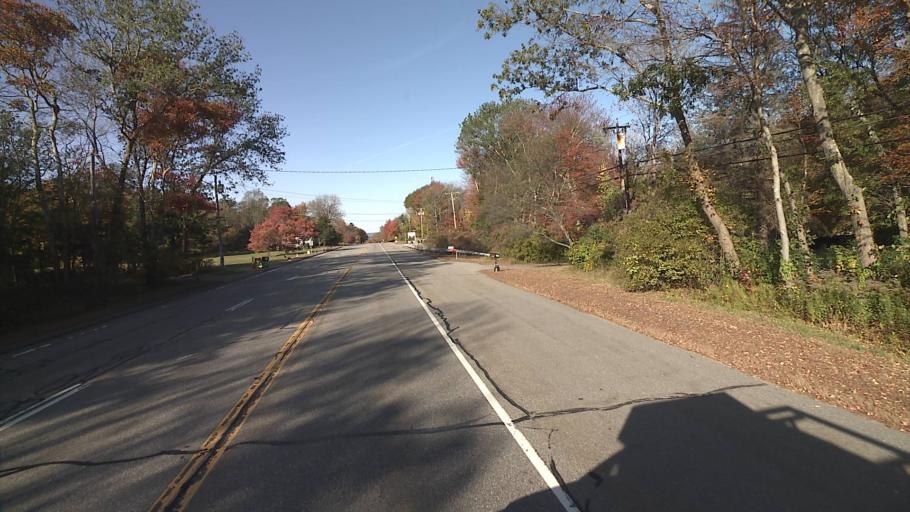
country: US
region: Connecticut
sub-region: Windham County
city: Danielson
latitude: 41.7909
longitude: -71.8176
